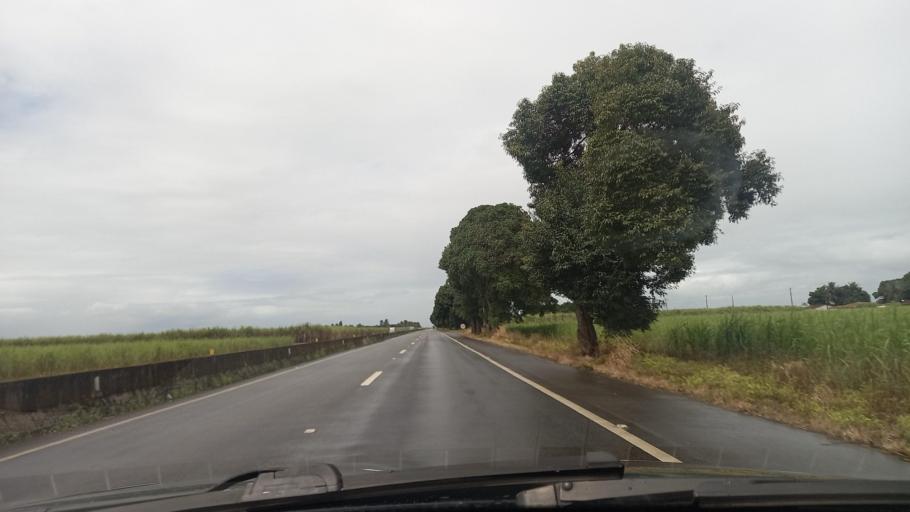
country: BR
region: Alagoas
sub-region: Campo Alegre
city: Campo Alegre
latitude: -9.8111
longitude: -36.2568
